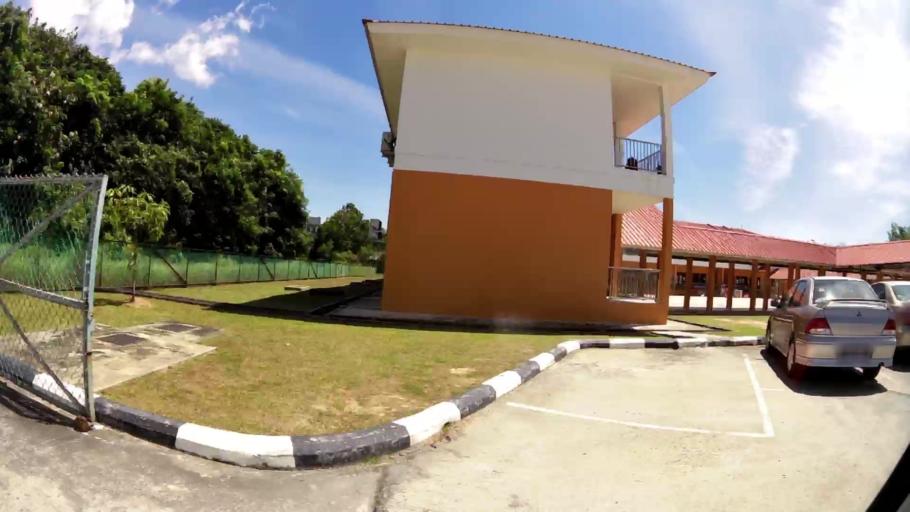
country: BN
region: Brunei and Muara
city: Bandar Seri Begawan
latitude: 4.9351
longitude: 114.9485
